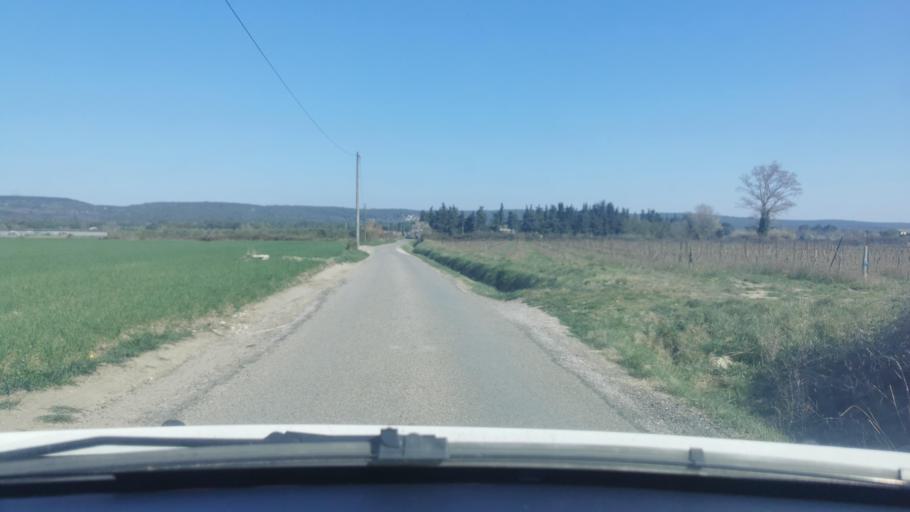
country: FR
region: Languedoc-Roussillon
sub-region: Departement du Gard
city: Montaren-et-Saint-Mediers
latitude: 44.0360
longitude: 4.3893
